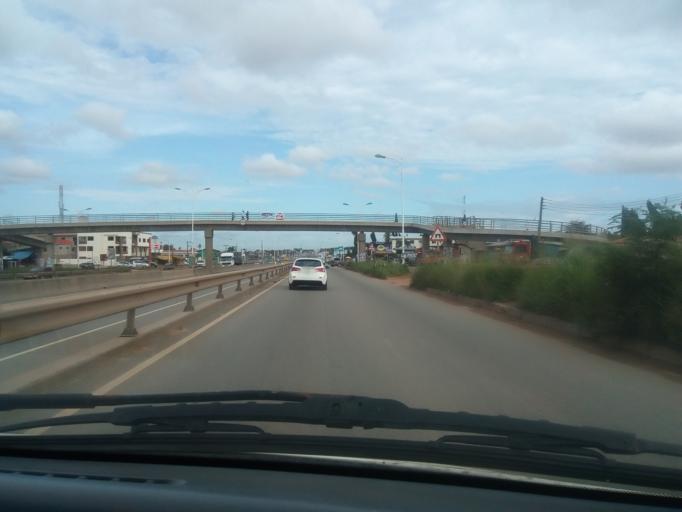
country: GH
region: Greater Accra
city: Dome
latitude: 5.6539
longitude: -0.2600
